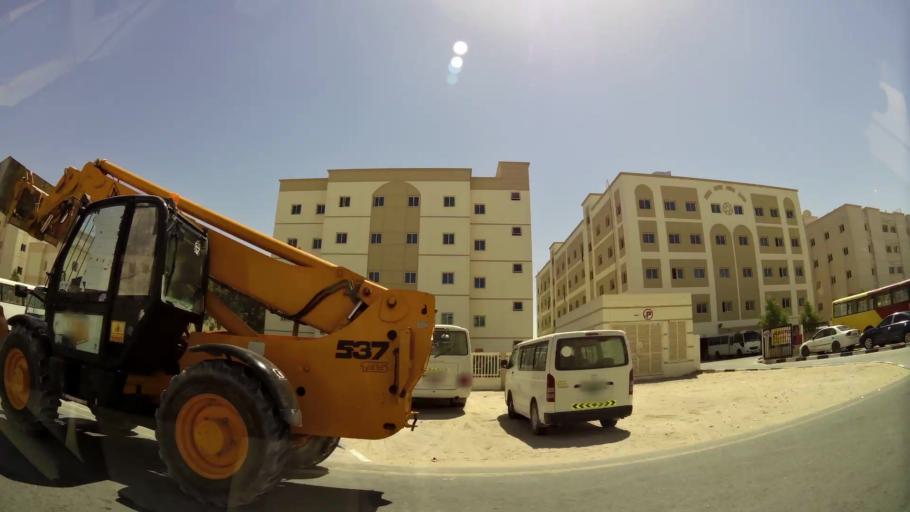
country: AE
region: Dubai
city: Dubai
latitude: 24.9771
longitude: 55.2045
